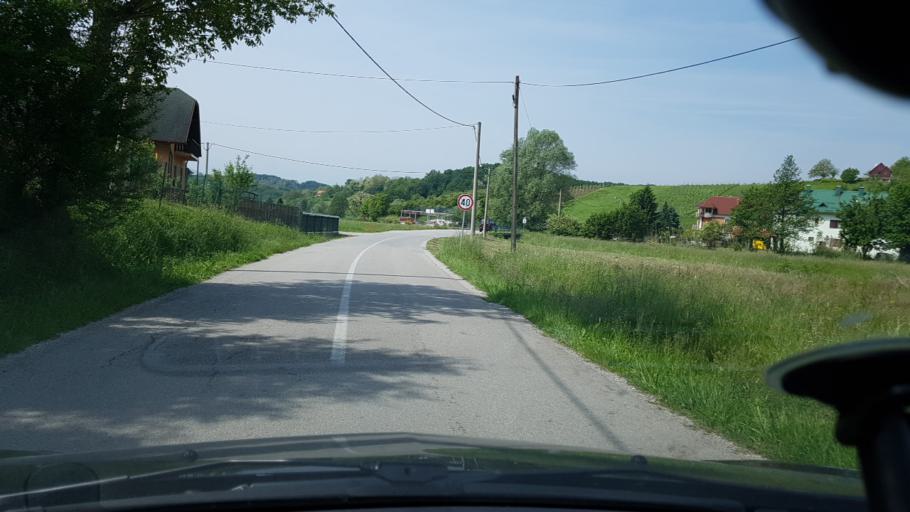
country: HR
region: Krapinsko-Zagorska
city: Marija Bistrica
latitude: 45.9315
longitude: 16.1957
